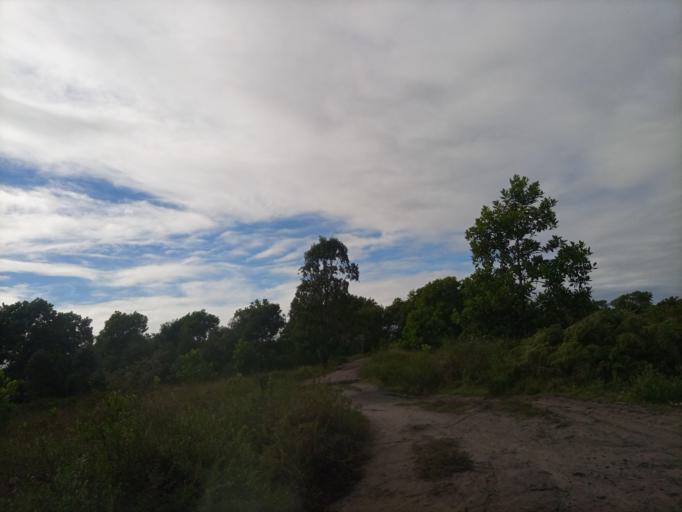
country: MG
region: Anosy
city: Fort Dauphin
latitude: -24.7789
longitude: 47.1875
